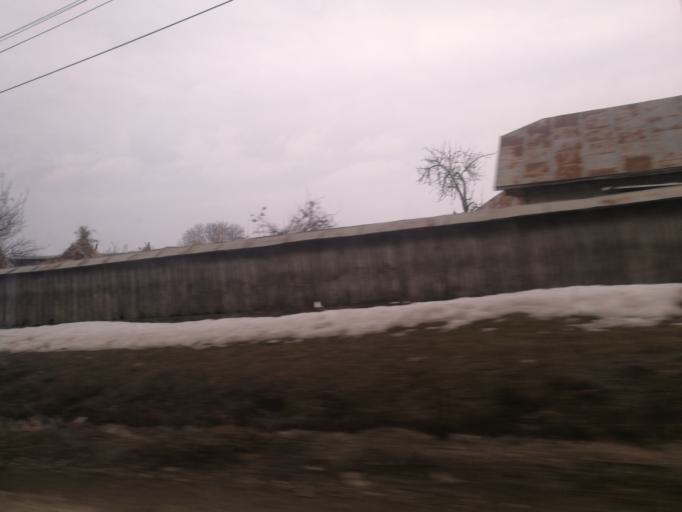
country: RO
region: Iasi
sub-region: Comuna Ruginoasa
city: Dumbravita
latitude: 47.2396
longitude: 26.8250
